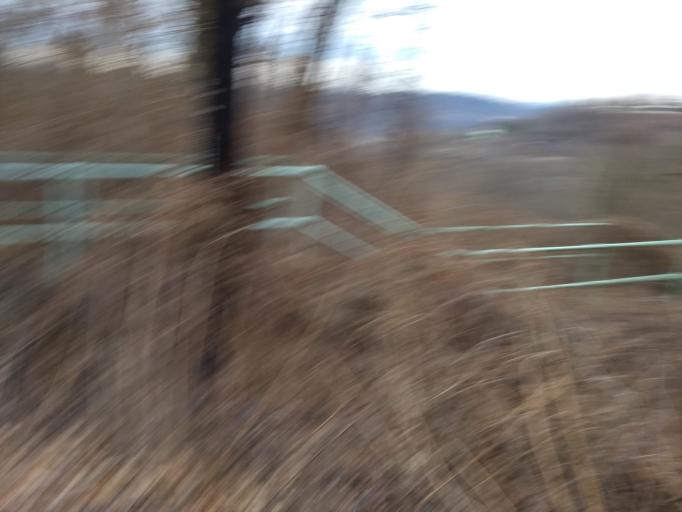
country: US
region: Pennsylvania
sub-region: Allegheny County
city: Homestead
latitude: 40.4119
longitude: -79.9347
